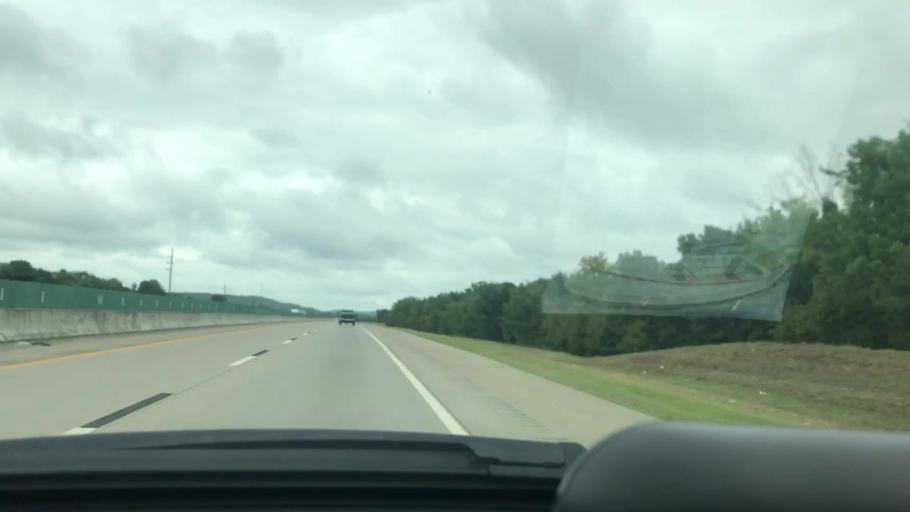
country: US
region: Oklahoma
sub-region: Pittsburg County
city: Krebs
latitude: 35.0347
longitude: -95.7126
